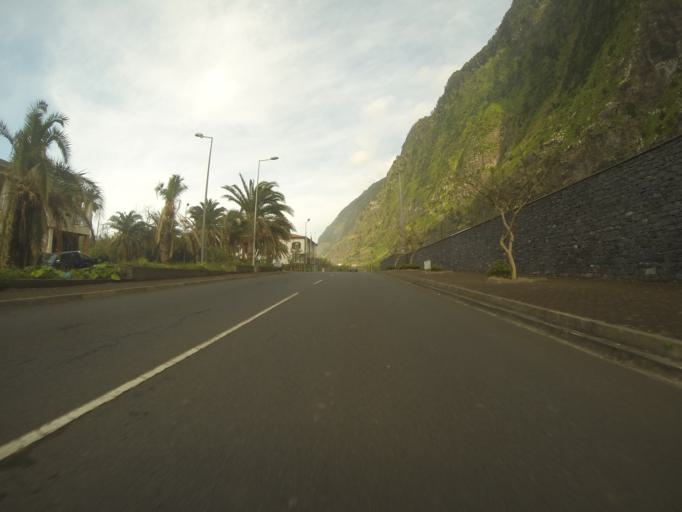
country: PT
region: Madeira
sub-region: Sao Vicente
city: Sao Vicente
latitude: 32.8111
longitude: -17.0422
